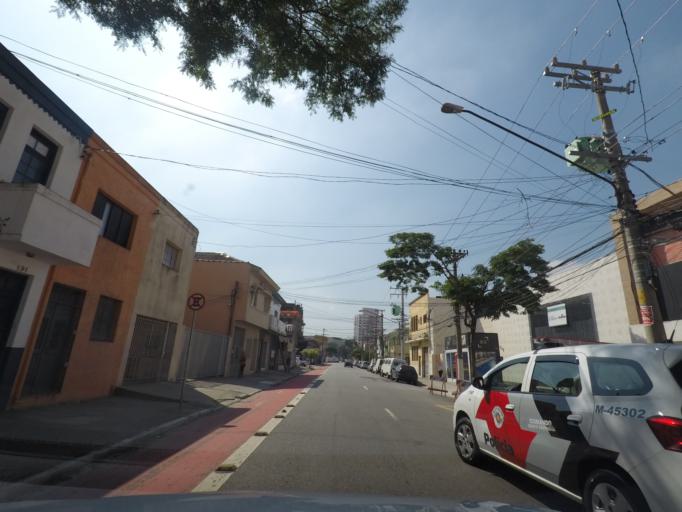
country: BR
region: Sao Paulo
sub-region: Sao Paulo
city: Sao Paulo
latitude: -23.5467
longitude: -46.5894
